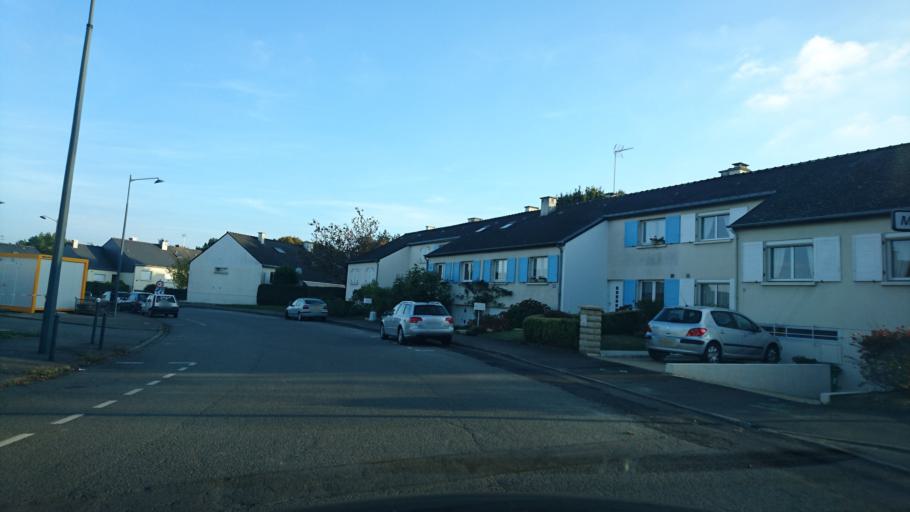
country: FR
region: Brittany
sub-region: Departement d'Ille-et-Vilaine
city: Chantepie
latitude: 48.0834
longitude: -1.6509
